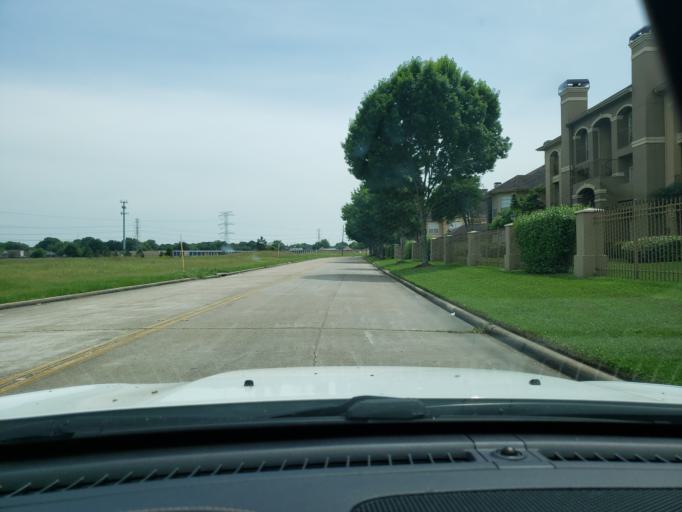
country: US
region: Texas
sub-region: Harris County
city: Jersey Village
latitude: 29.9134
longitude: -95.5812
